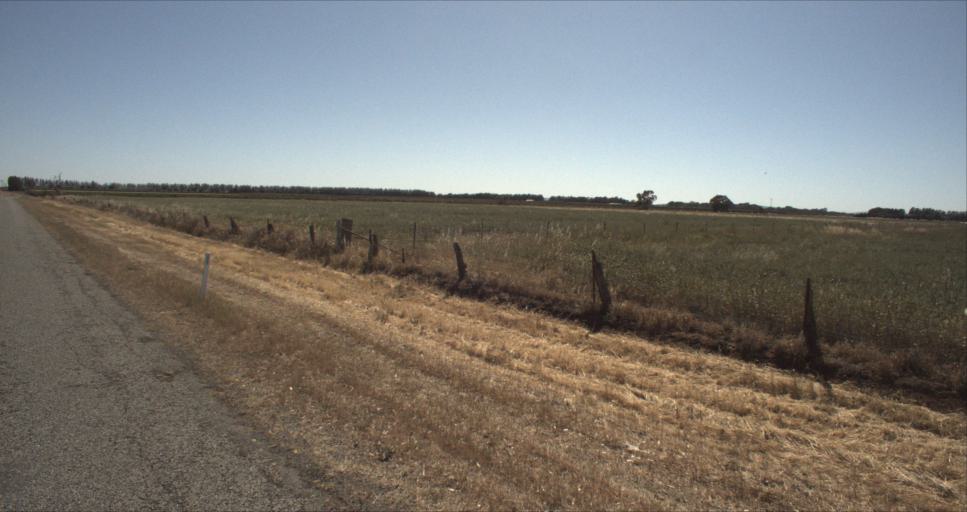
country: AU
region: New South Wales
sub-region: Leeton
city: Leeton
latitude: -34.5349
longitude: 146.3176
